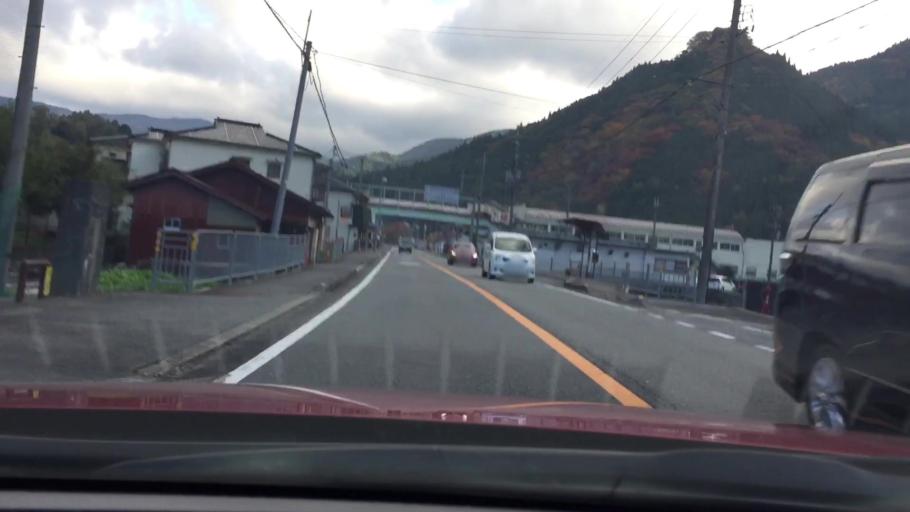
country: JP
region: Hyogo
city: Yamazakicho-nakabirose
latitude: 35.1539
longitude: 134.5443
